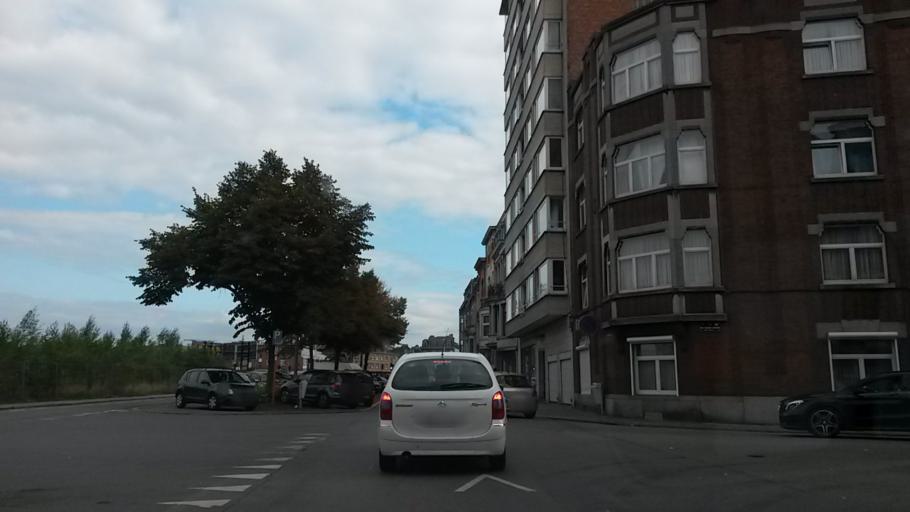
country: BE
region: Wallonia
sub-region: Province de Liege
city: Liege
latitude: 50.6429
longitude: 5.5891
